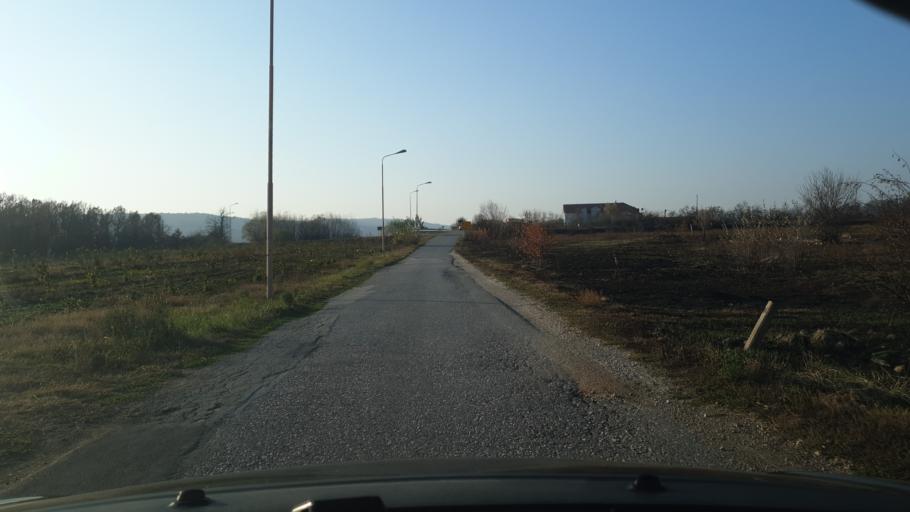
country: RS
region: Central Serbia
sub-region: Zajecarski Okrug
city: Zajecar
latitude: 44.0899
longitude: 22.3463
